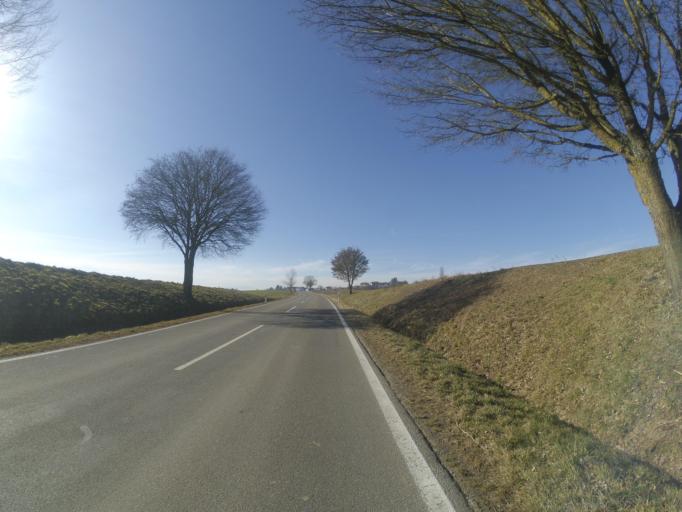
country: DE
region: Baden-Wuerttemberg
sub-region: Tuebingen Region
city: Wolpertswende
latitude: 47.9231
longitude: 9.6313
